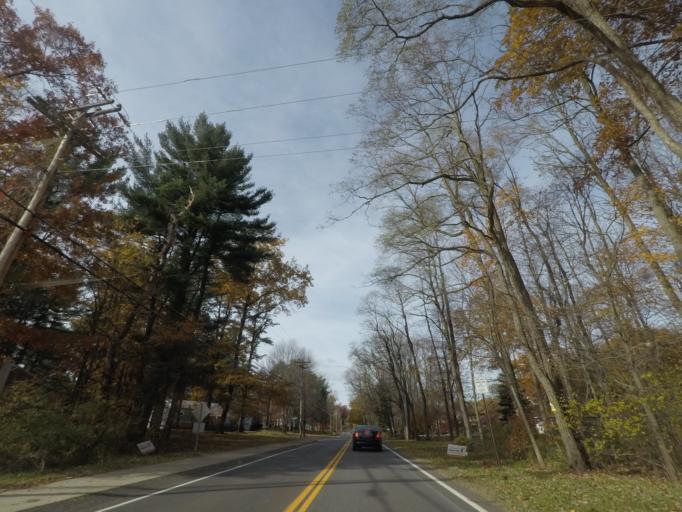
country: US
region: New York
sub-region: Schenectady County
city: Rotterdam
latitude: 42.7414
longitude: -73.9210
